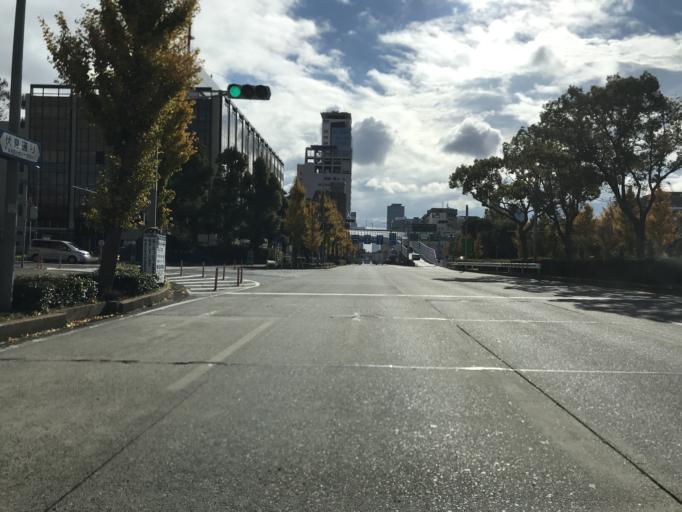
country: JP
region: Aichi
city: Nagoya-shi
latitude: 35.1801
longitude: 136.8964
